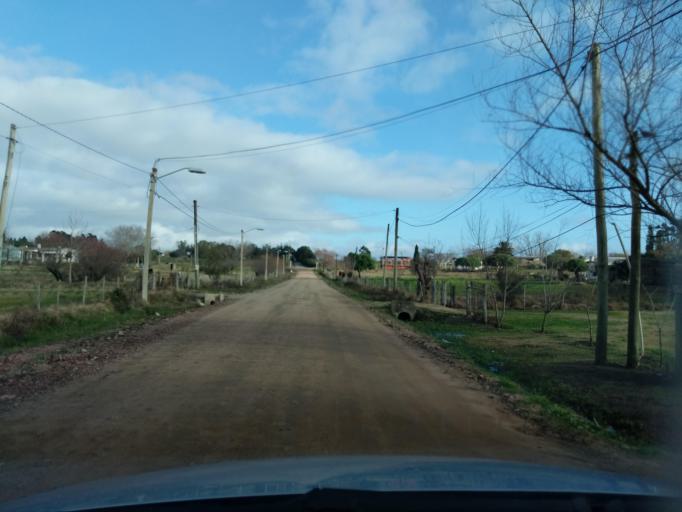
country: UY
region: Florida
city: Florida
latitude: -34.0804
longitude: -56.2095
